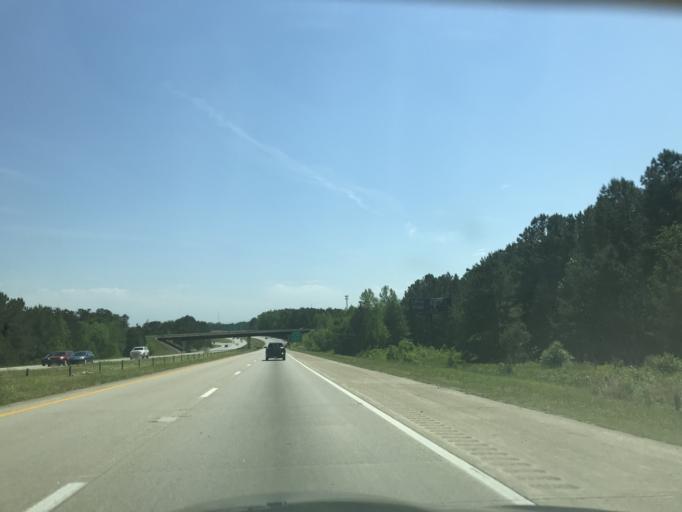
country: US
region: North Carolina
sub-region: Johnston County
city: Benson
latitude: 35.4006
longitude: -78.5231
